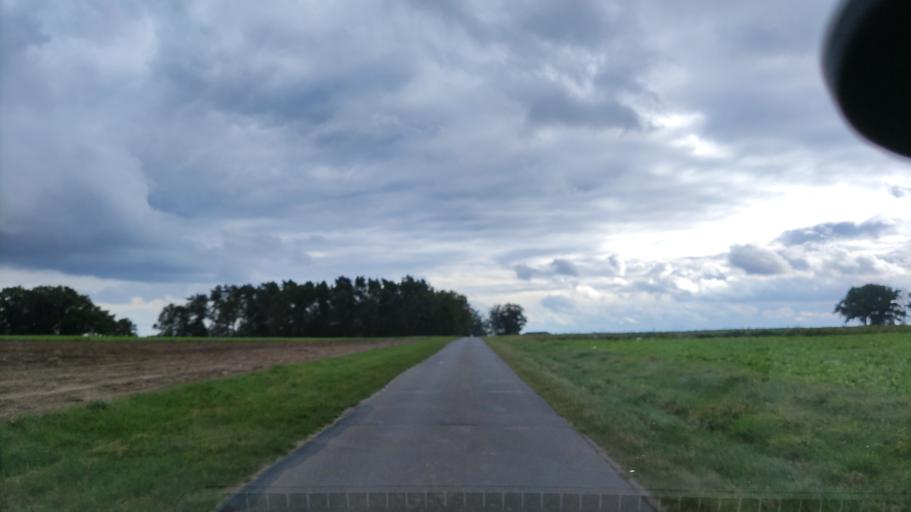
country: DE
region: Lower Saxony
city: Vastorf
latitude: 53.1598
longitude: 10.5339
